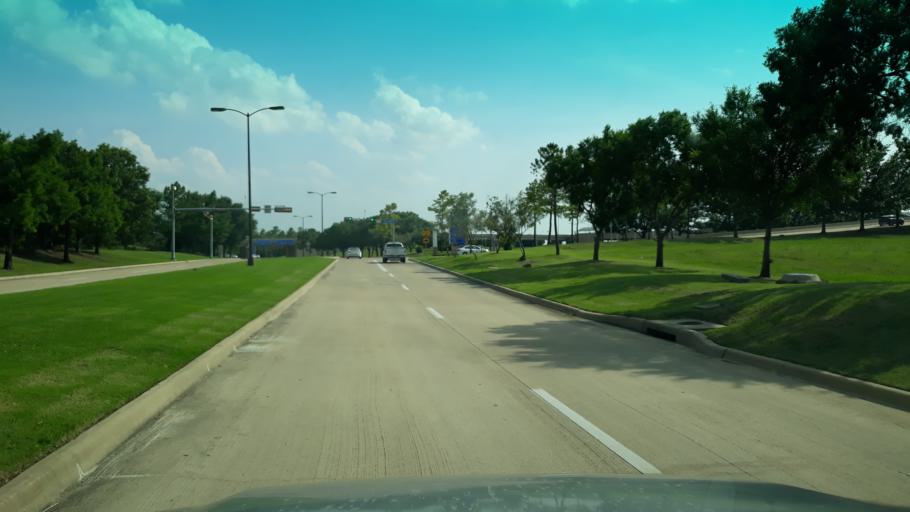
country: US
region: Texas
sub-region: Tarrant County
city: Euless
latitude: 32.8582
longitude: -97.0319
